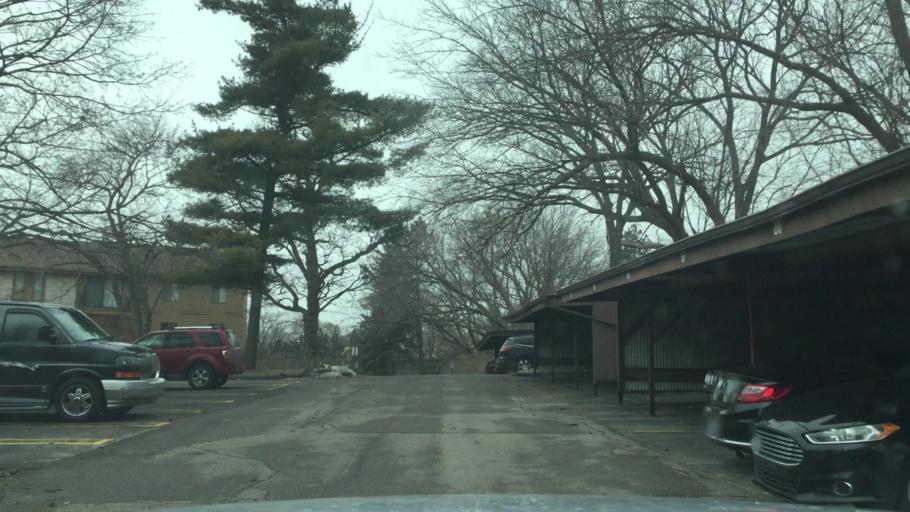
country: US
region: Michigan
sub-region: Oakland County
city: Franklin
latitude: 42.5048
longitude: -83.3084
